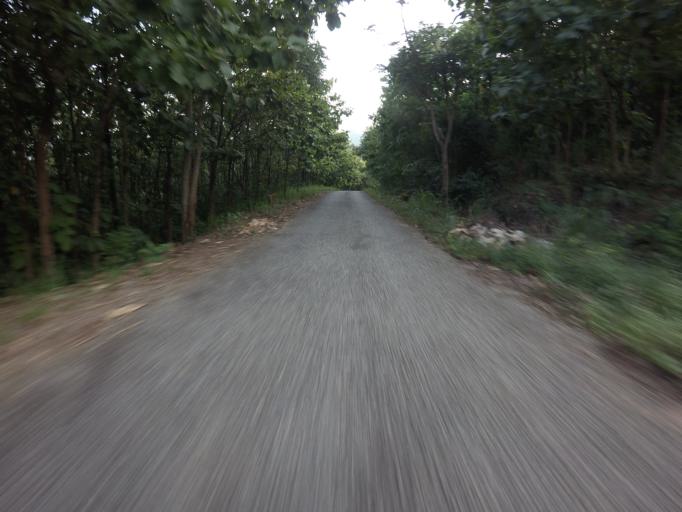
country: TG
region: Plateaux
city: Kpalime
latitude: 6.8864
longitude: 0.4472
